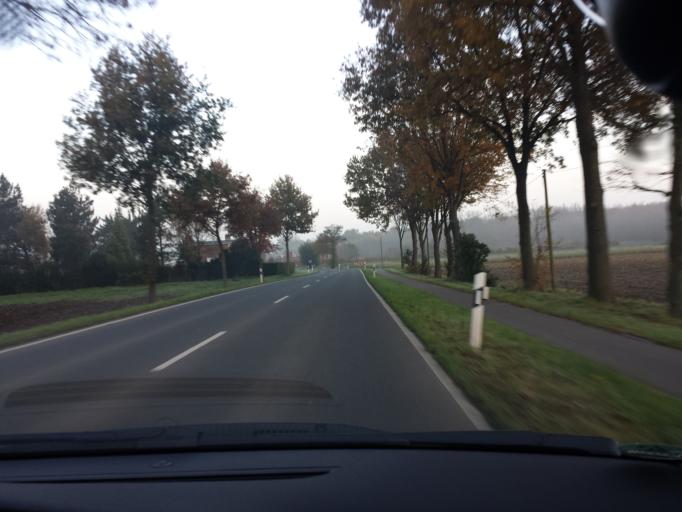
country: NL
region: Limburg
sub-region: Gemeente Sittard-Geleen
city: Limbricht
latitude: 51.0497
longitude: 5.8675
